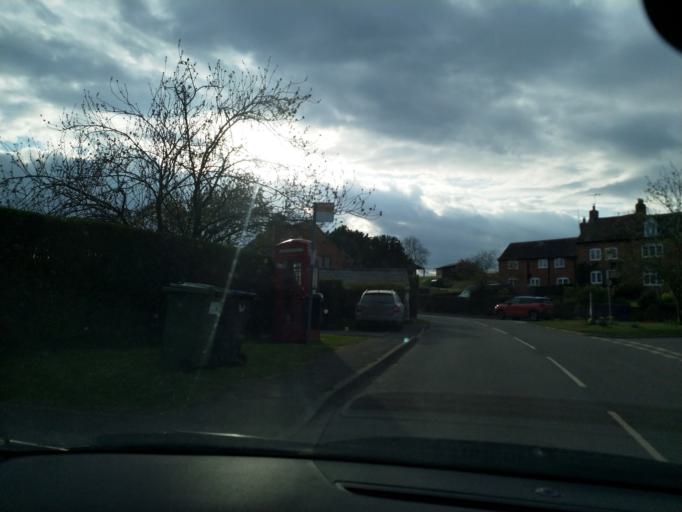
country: GB
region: England
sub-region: Warwickshire
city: Wellesbourne Mountford
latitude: 52.2171
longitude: -1.5545
